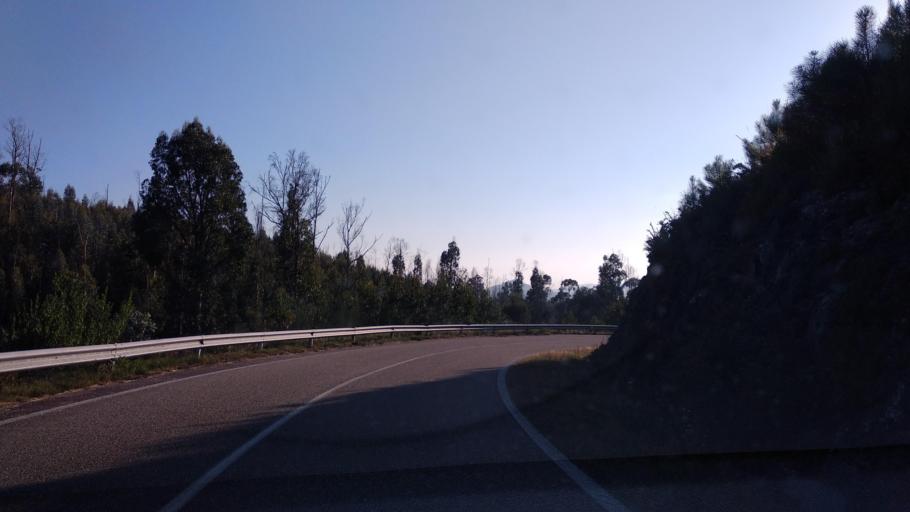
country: ES
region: Galicia
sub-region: Provincia de Pontevedra
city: Ponte Caldelas
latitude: 42.3585
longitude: -8.5264
